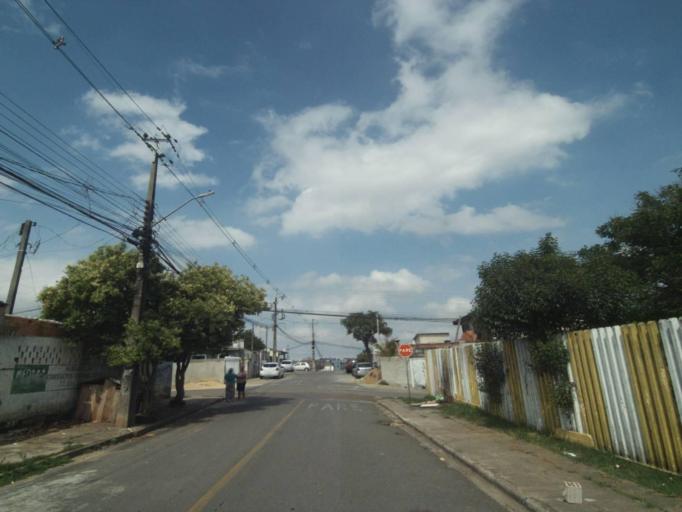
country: BR
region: Parana
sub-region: Curitiba
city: Curitiba
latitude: -25.5010
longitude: -49.3474
